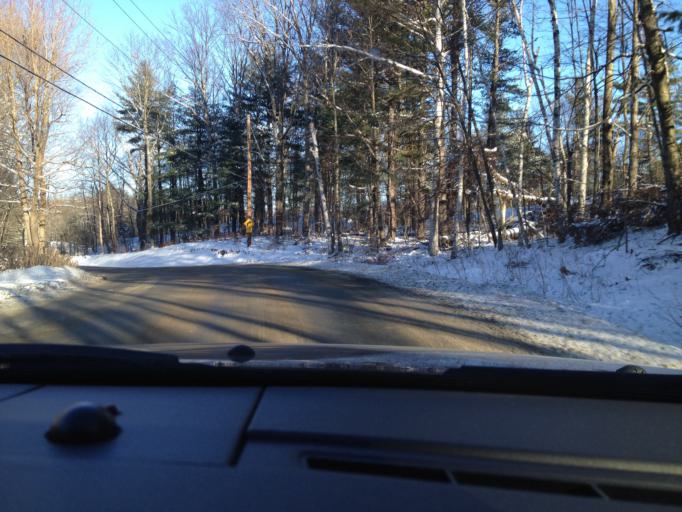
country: US
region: New York
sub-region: Rensselaer County
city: Averill Park
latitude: 42.6238
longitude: -73.5795
